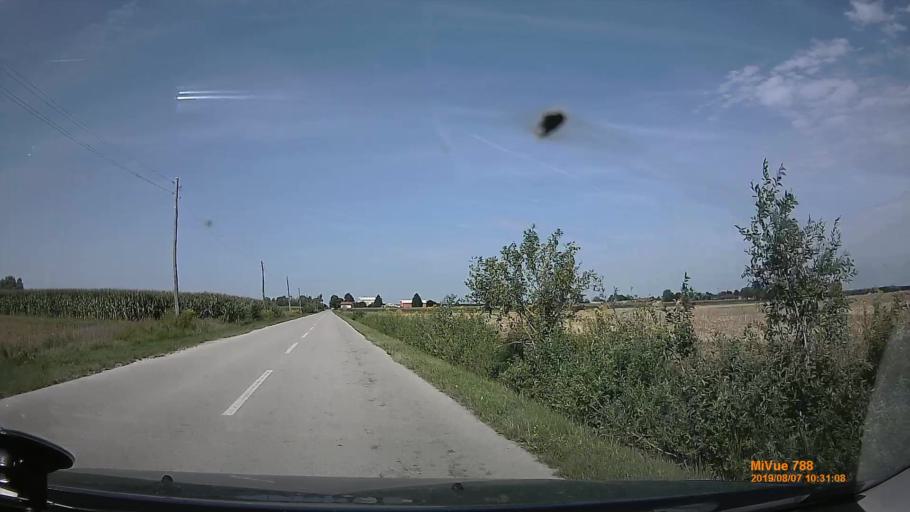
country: SI
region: Lendava-Lendva
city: Lendava
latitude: 46.6168
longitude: 16.4139
